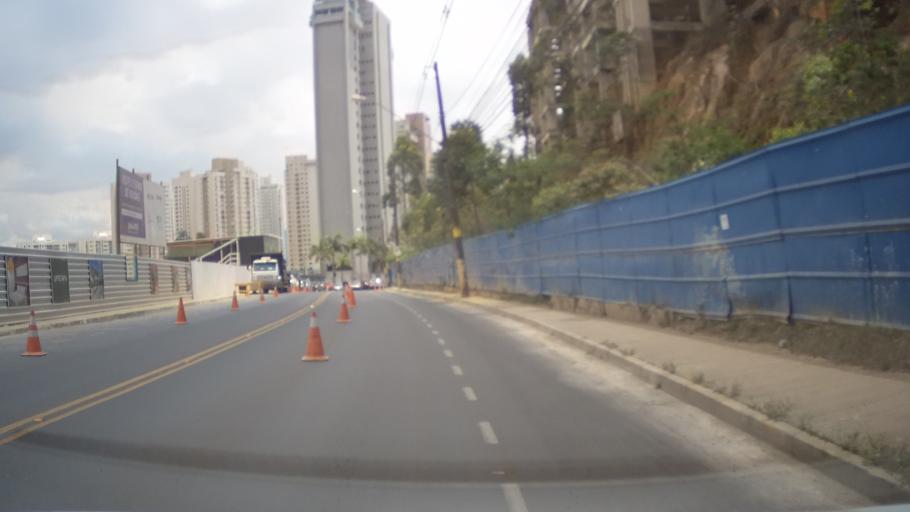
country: BR
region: Minas Gerais
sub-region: Belo Horizonte
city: Belo Horizonte
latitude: -19.9731
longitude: -43.9300
